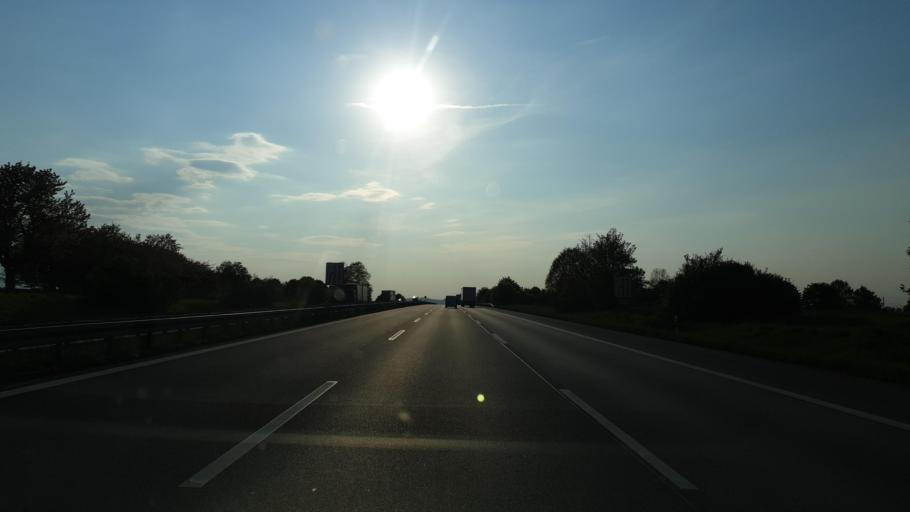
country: DE
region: Saxony
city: Crostwitz
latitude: 51.2029
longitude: 14.2766
